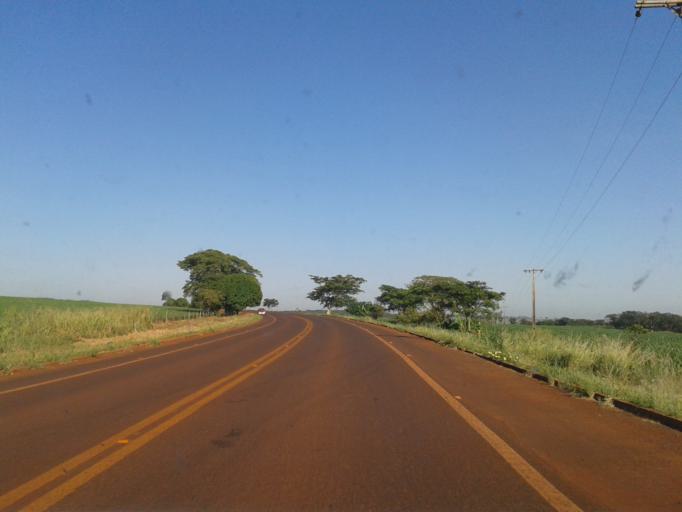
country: BR
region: Minas Gerais
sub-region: Capinopolis
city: Capinopolis
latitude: -18.6834
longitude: -49.5937
